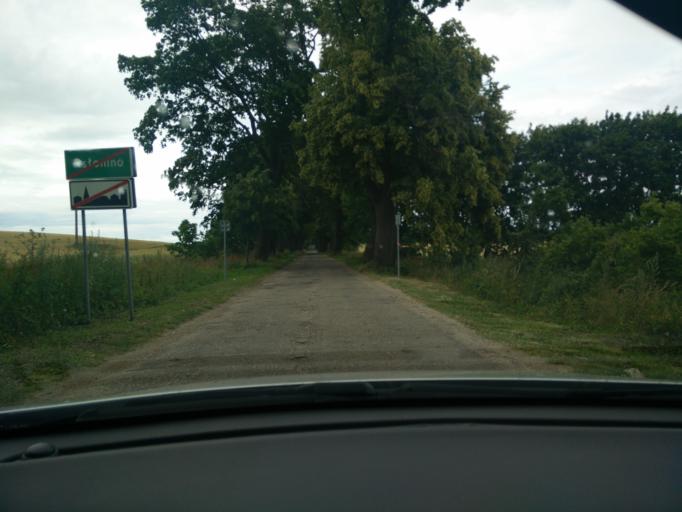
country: PL
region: Pomeranian Voivodeship
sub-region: Powiat pucki
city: Mrzezino
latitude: 54.6700
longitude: 18.4572
